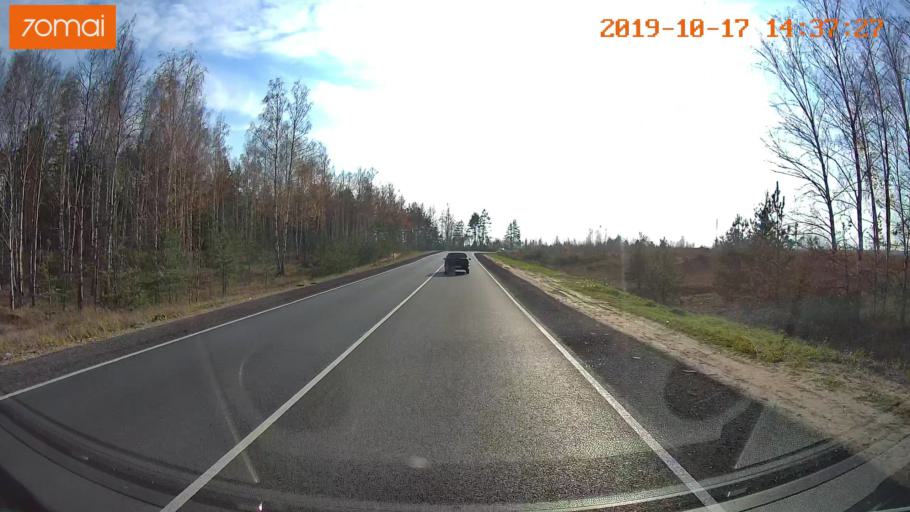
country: RU
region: Rjazan
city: Solotcha
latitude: 54.8794
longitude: 39.9956
